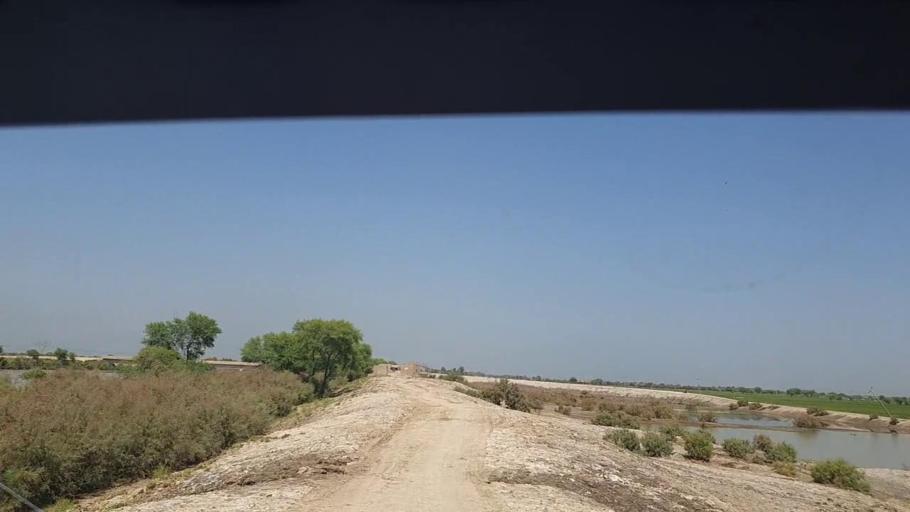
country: PK
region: Sindh
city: Kandhkot
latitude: 28.1876
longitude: 69.1605
